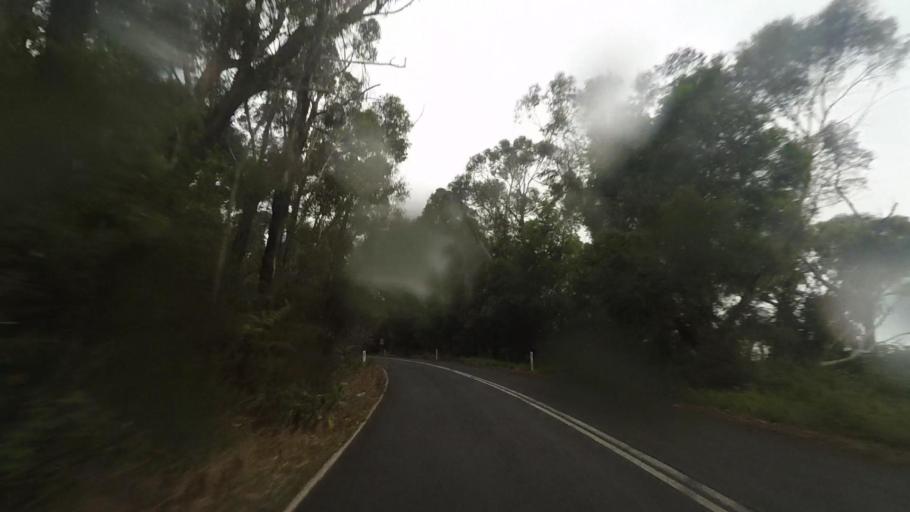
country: AU
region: New South Wales
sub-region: Wollongong
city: Mount Keira
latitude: -34.3976
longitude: 150.8447
